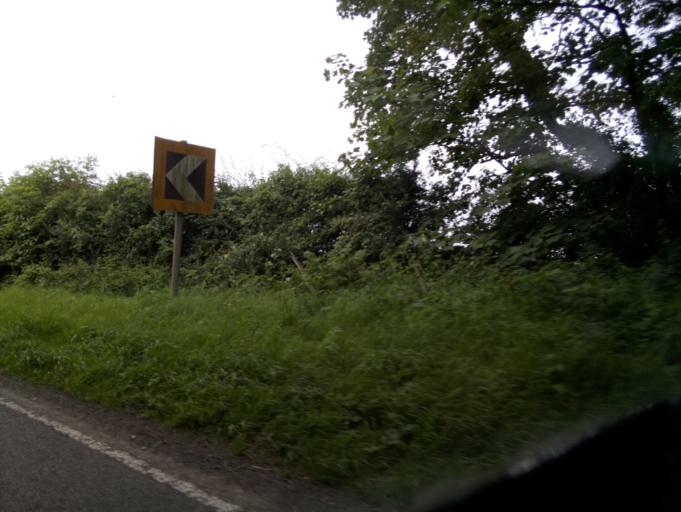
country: GB
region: England
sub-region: Somerset
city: Street
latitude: 51.0801
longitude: -2.6895
